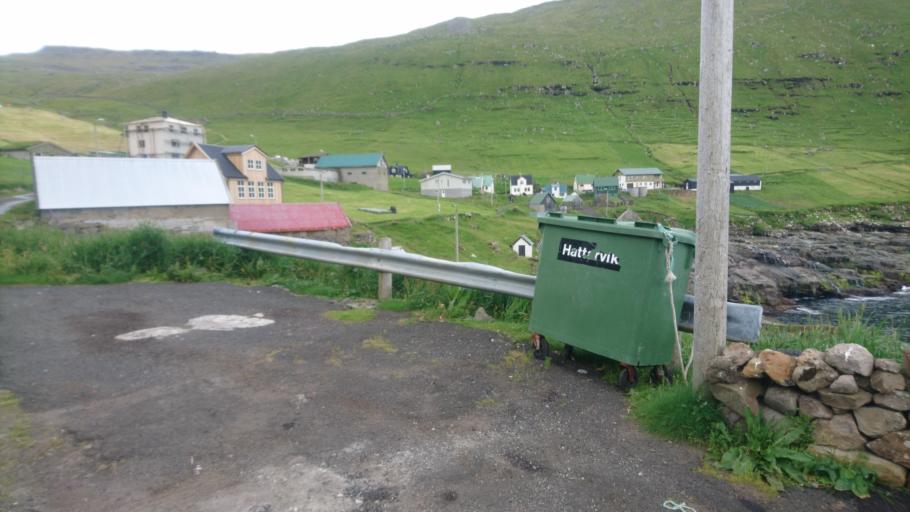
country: FO
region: Nordoyar
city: Klaksvik
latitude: 62.3286
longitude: -6.2767
